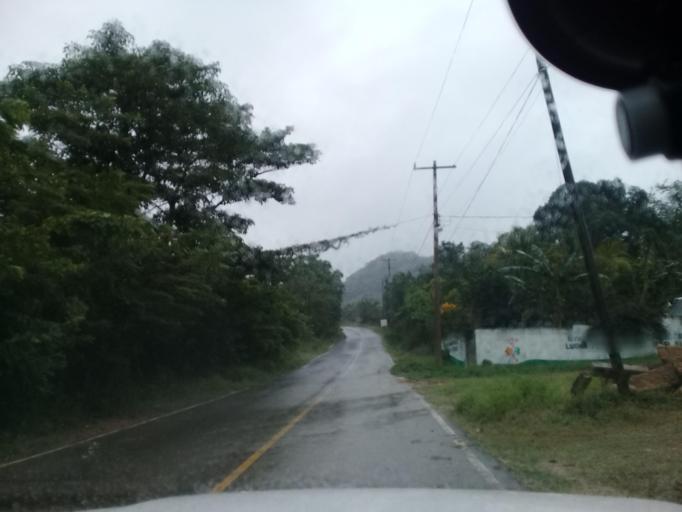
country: MX
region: Veracruz
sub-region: Chalma
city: San Pedro Coyutla
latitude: 21.2312
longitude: -98.4540
